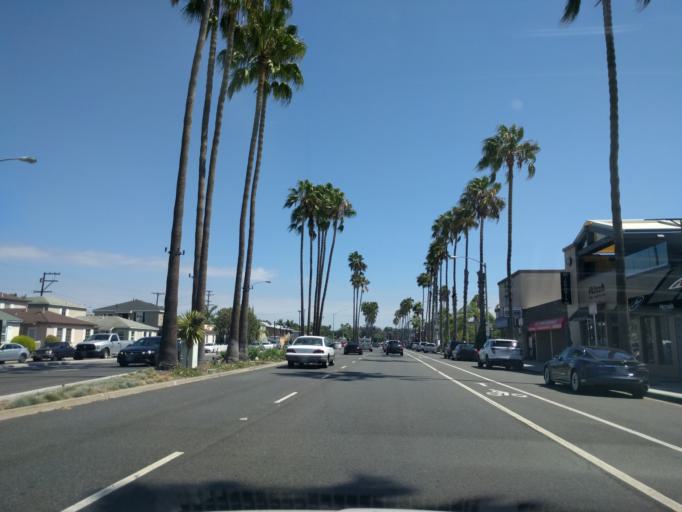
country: US
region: California
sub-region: Orange County
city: Seal Beach
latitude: 33.7572
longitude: -118.1250
